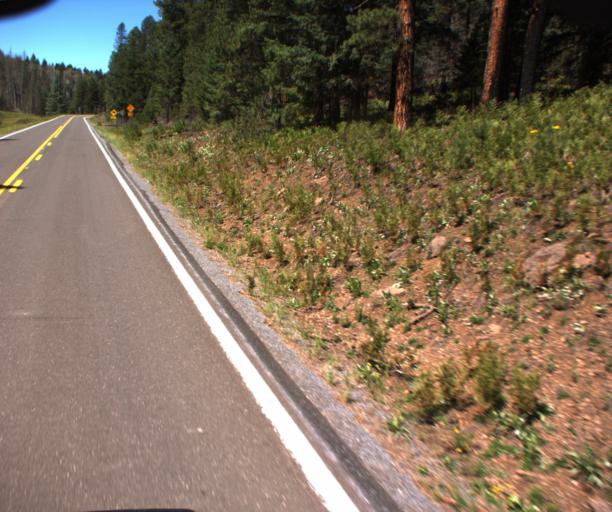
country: US
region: Arizona
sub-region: Apache County
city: Eagar
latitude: 33.6443
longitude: -109.3160
